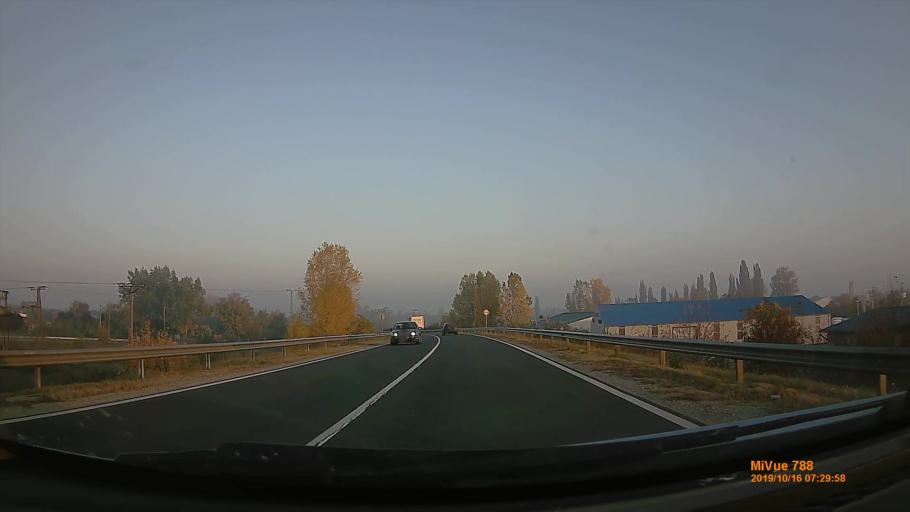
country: HU
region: Heves
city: Fuzesabony
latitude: 47.7379
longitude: 20.4089
